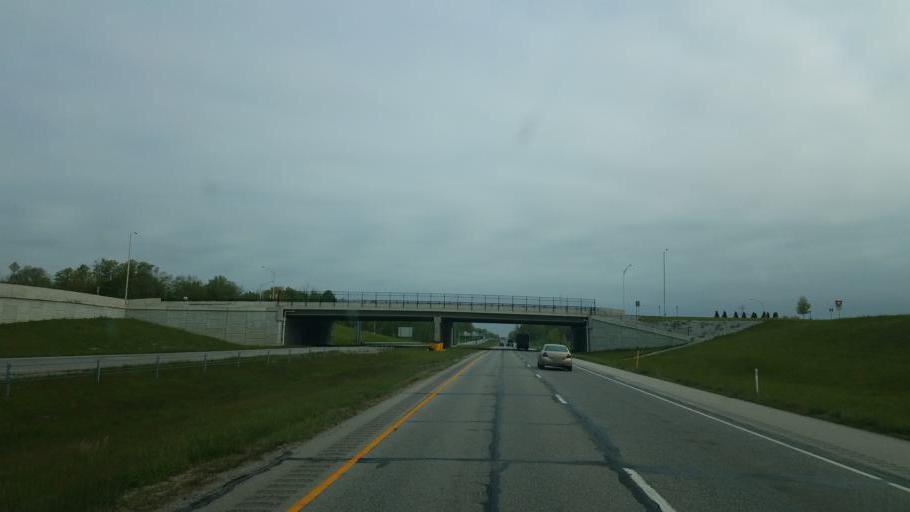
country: US
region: Indiana
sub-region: Allen County
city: Fort Wayne
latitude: 41.1988
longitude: -85.1041
